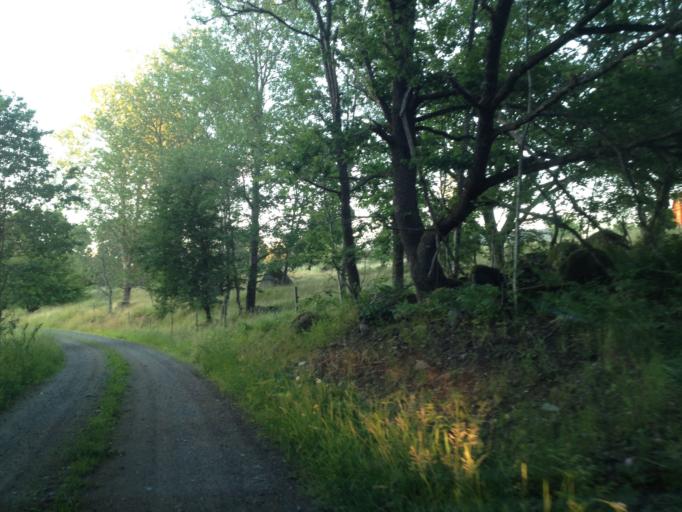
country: SE
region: Kalmar
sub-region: Vasterviks Kommun
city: Overum
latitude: 58.0187
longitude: 16.1202
